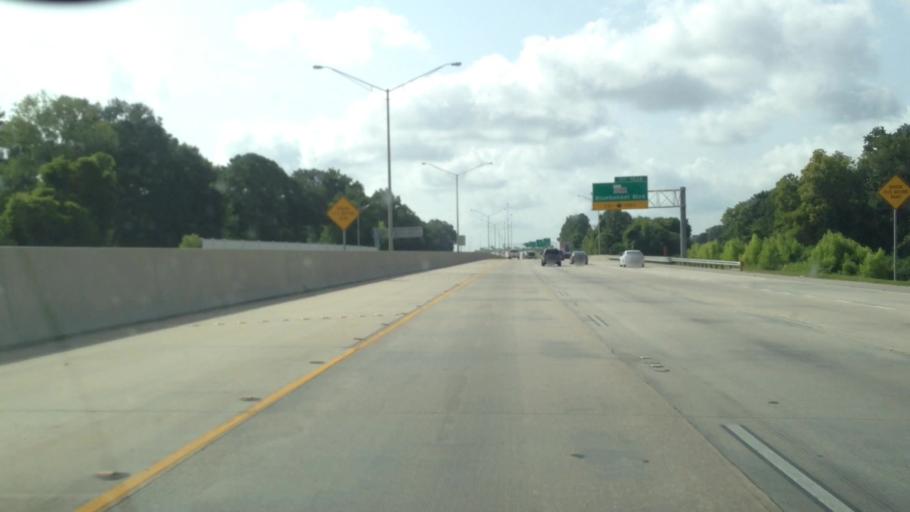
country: US
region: Louisiana
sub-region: East Baton Rouge Parish
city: Inniswold
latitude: 30.4020
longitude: -91.0944
